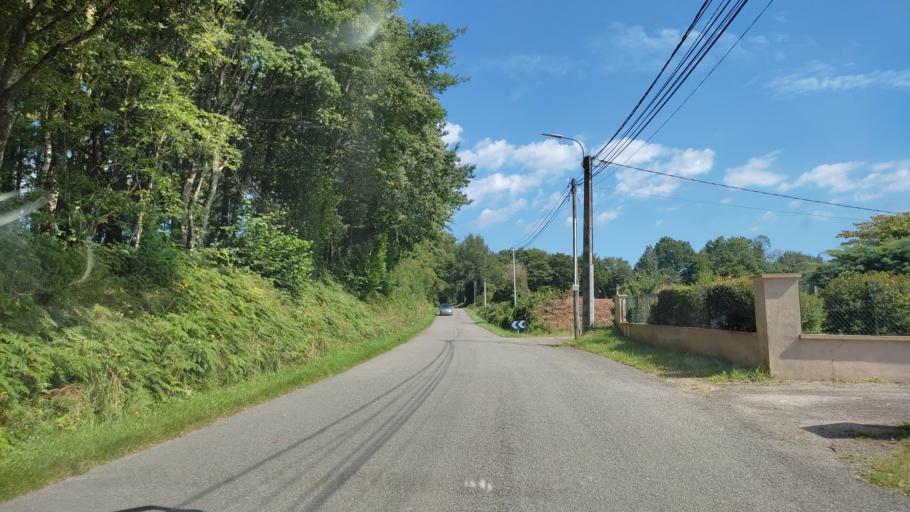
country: FR
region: Limousin
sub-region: Departement de la Haute-Vienne
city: Isle
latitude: 45.8484
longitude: 1.1926
